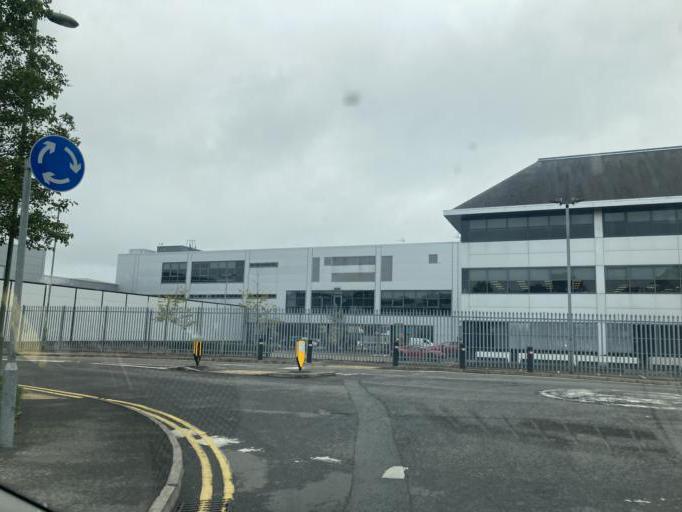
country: GB
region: England
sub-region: Bracknell Forest
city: Sandhurst
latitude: 51.3333
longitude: -0.7684
